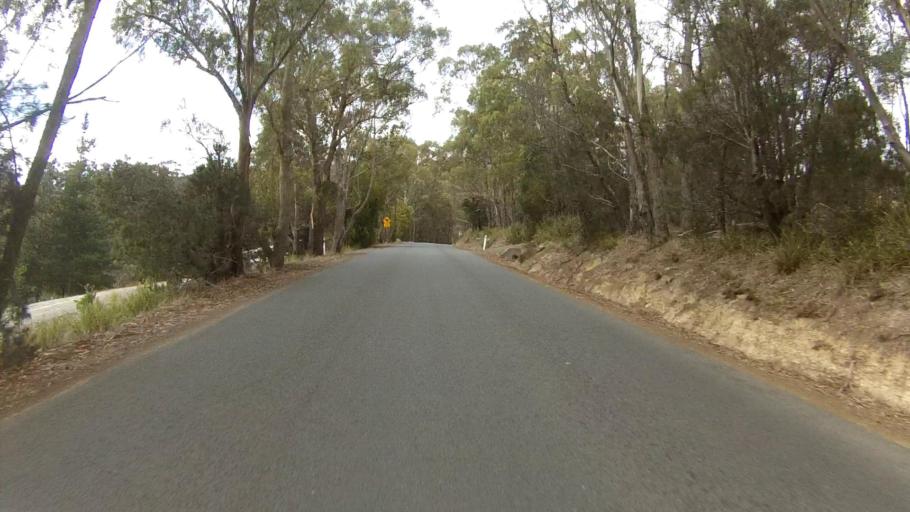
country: AU
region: Tasmania
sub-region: Kingborough
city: Blackmans Bay
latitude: -43.0231
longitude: 147.3082
